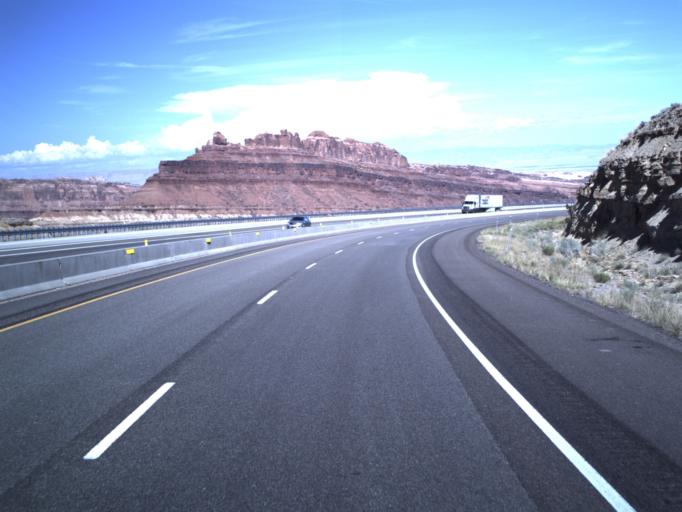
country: US
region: Utah
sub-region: Emery County
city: Castle Dale
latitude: 38.9374
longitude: -110.4855
